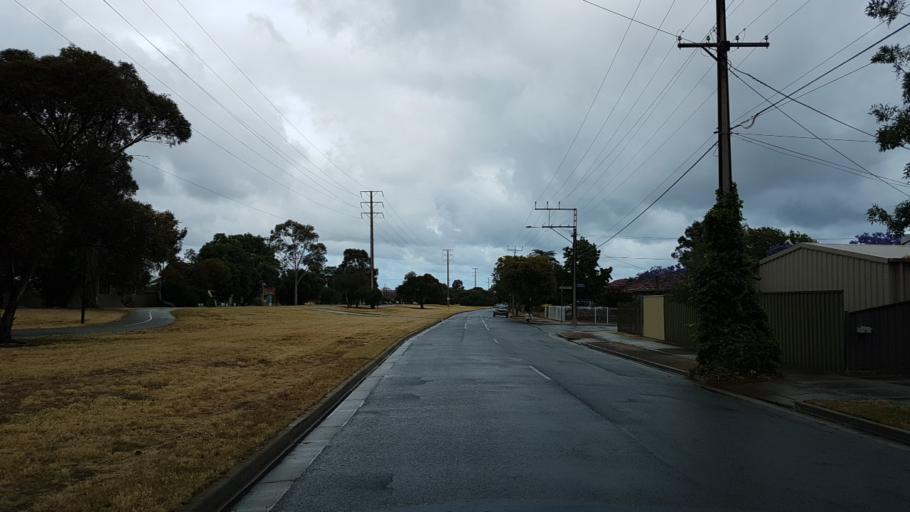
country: AU
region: South Australia
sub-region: City of West Torrens
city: Plympton
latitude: -34.9619
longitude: 138.5527
